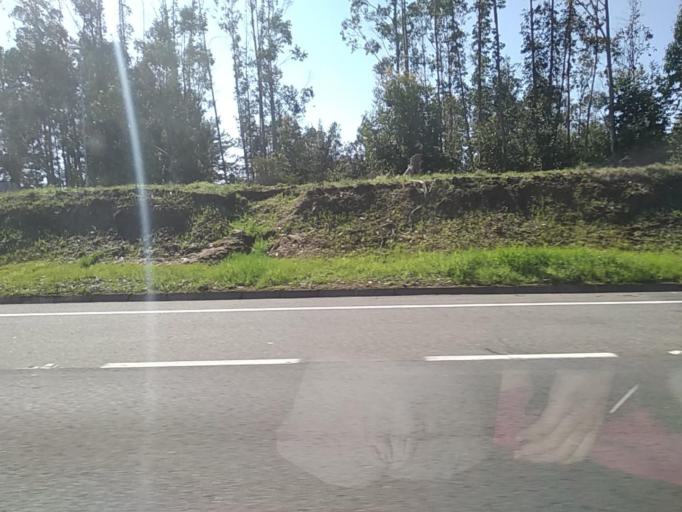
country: CL
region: Valparaiso
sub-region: San Antonio Province
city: El Tabo
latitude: -33.3996
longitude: -71.5885
